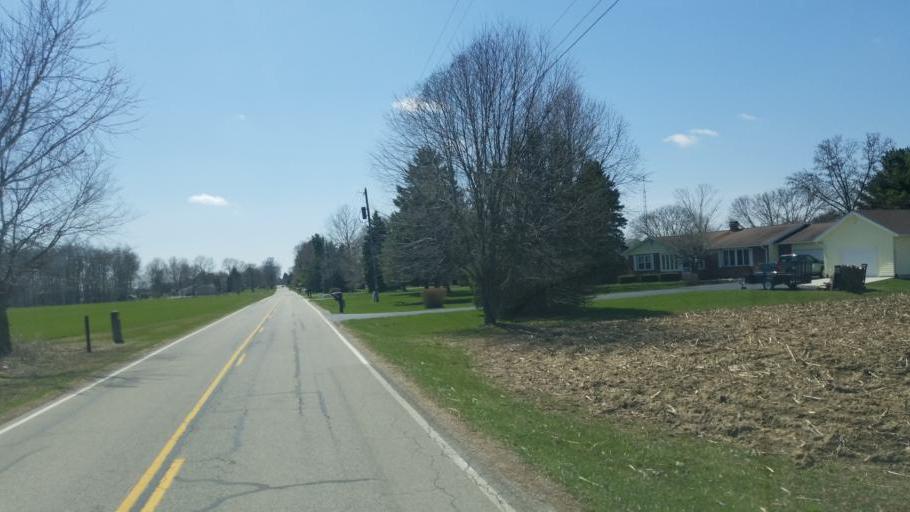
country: US
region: Ohio
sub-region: Marion County
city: Prospect
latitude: 40.4669
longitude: -83.1777
